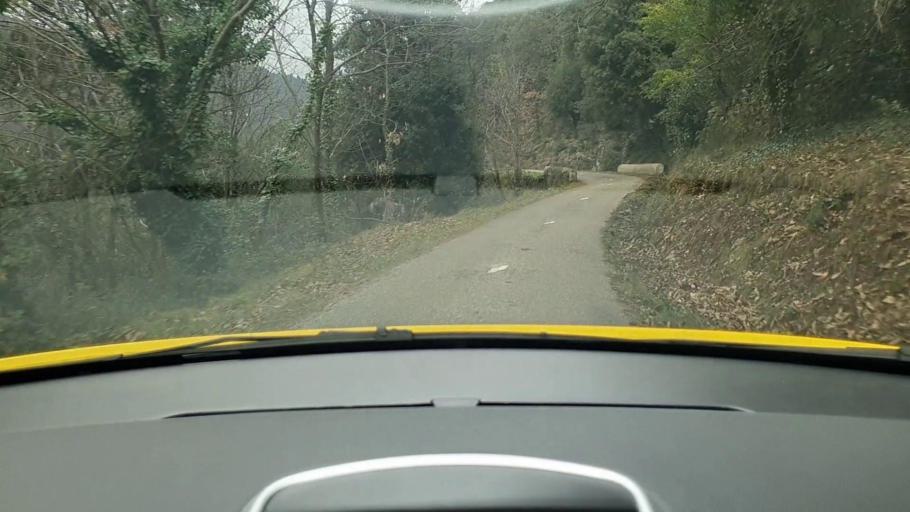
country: FR
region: Languedoc-Roussillon
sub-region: Departement du Gard
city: Besseges
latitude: 44.3683
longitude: 4.0444
